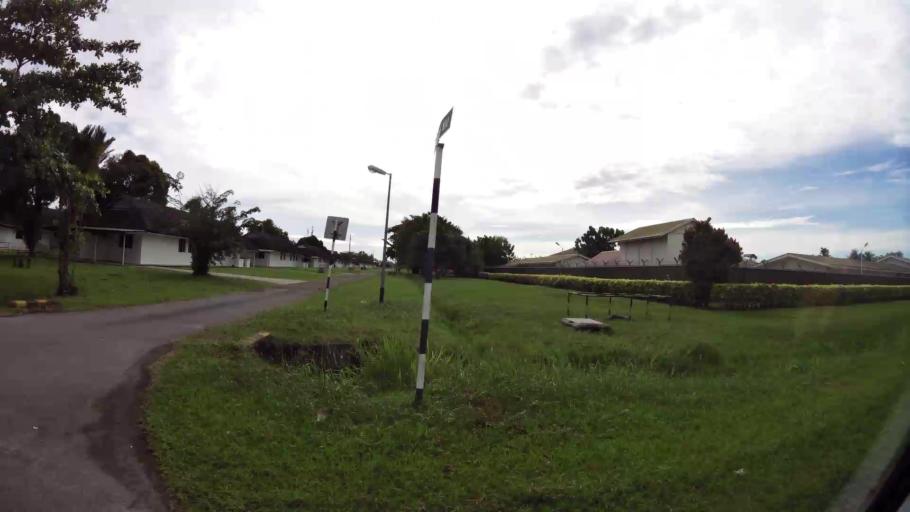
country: BN
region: Belait
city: Seria
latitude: 4.6089
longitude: 114.3239
